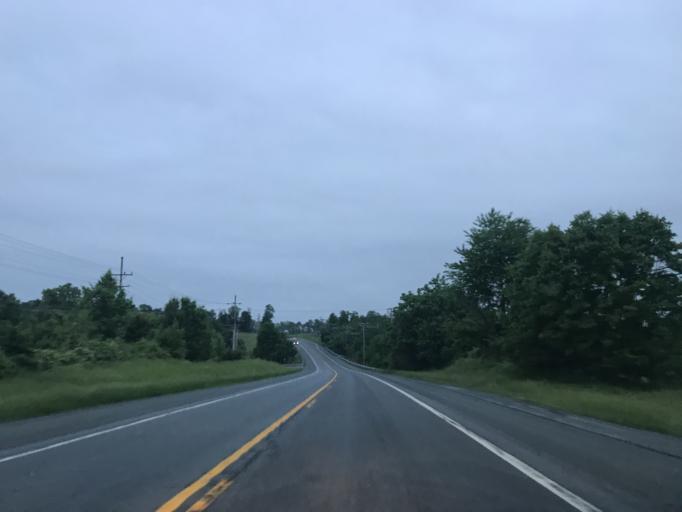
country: US
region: Maryland
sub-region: Frederick County
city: Linganore
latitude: 39.3977
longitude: -77.2608
